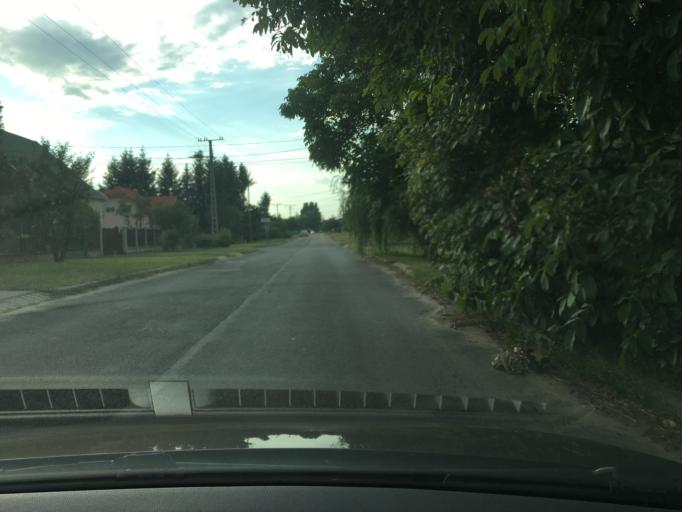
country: HU
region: Pest
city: Veresegyhaz
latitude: 47.6542
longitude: 19.2697
